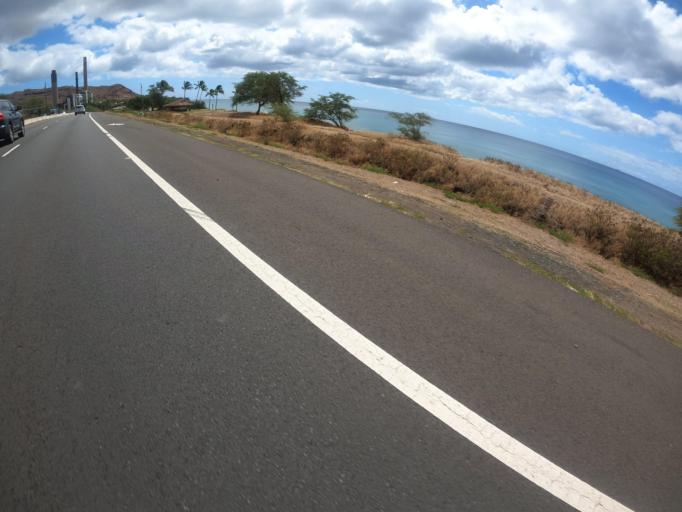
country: US
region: Hawaii
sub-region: Honolulu County
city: Nanakuli
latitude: 21.3624
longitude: -158.1323
